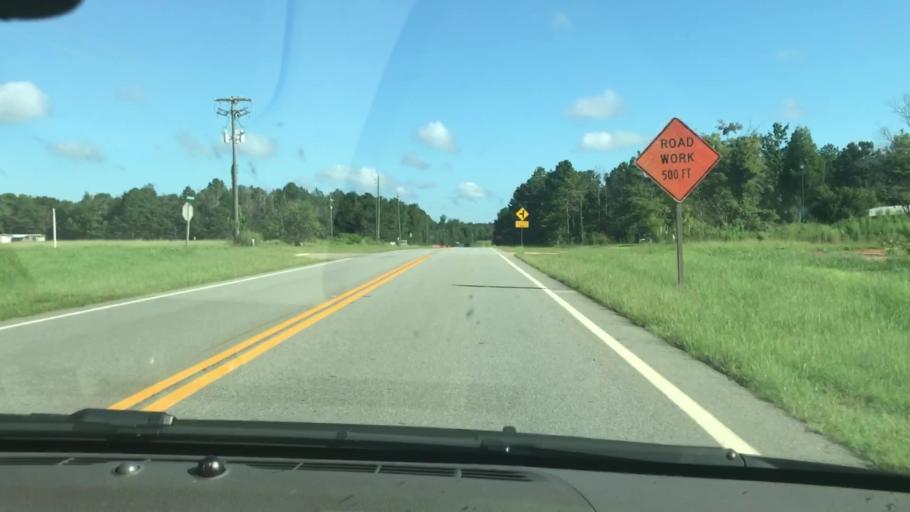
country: US
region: Georgia
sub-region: Quitman County
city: Georgetown
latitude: 31.8131
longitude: -85.0937
